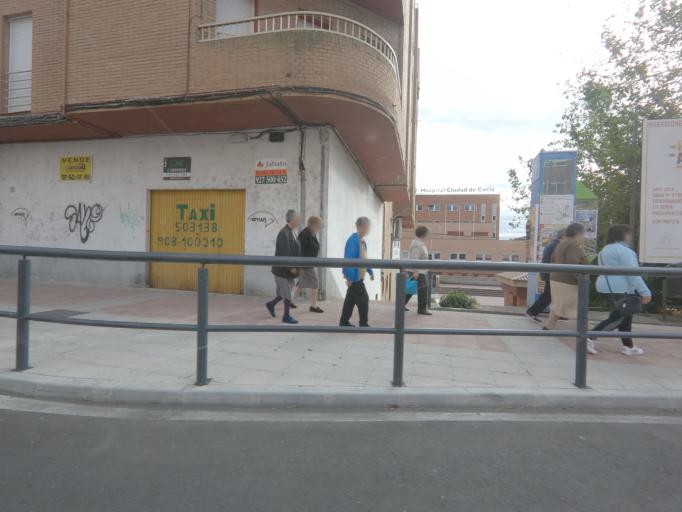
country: ES
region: Extremadura
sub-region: Provincia de Caceres
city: Coria
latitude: 39.9918
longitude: -6.5414
